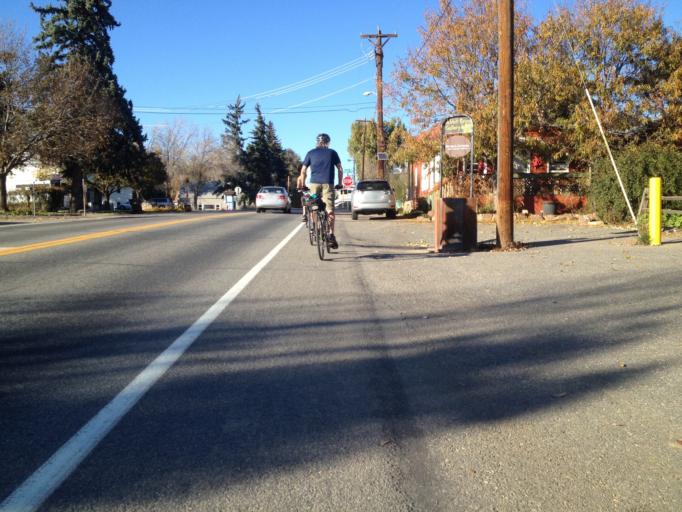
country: US
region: Colorado
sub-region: Boulder County
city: Longmont
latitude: 40.1881
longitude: -105.1781
